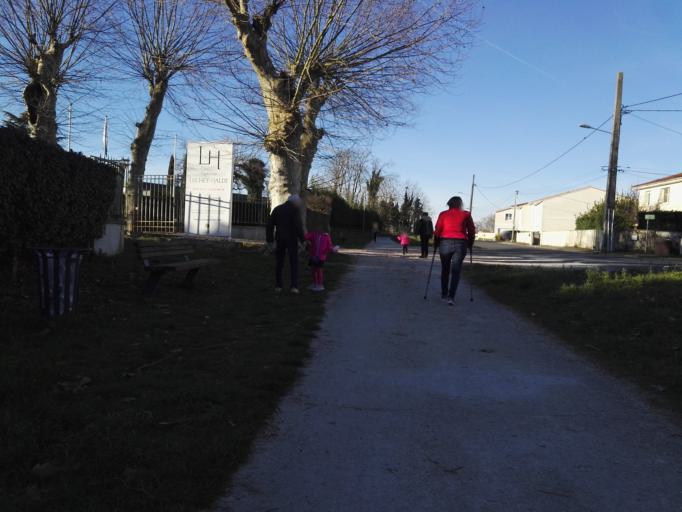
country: FR
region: Aquitaine
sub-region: Departement de la Gironde
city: Merignac
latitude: 44.8197
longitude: -0.6291
